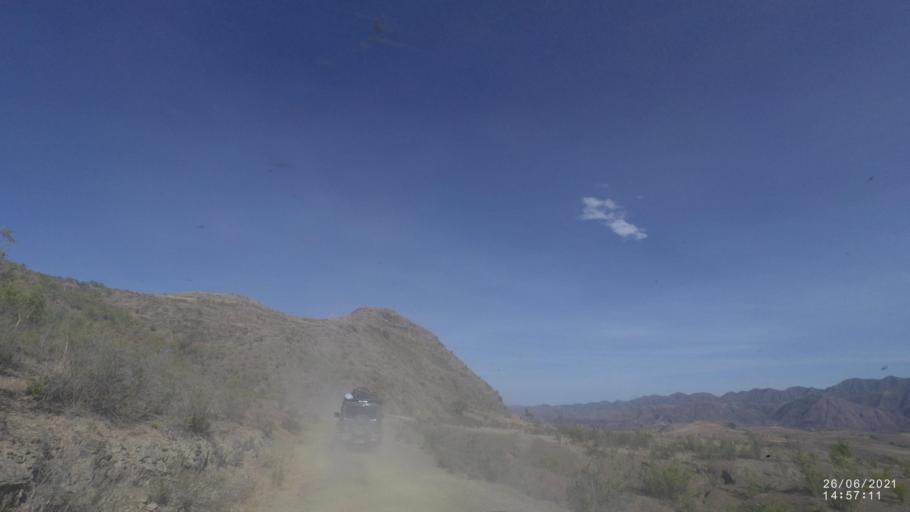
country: BO
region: Cochabamba
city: Mizque
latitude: -17.9409
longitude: -65.6202
